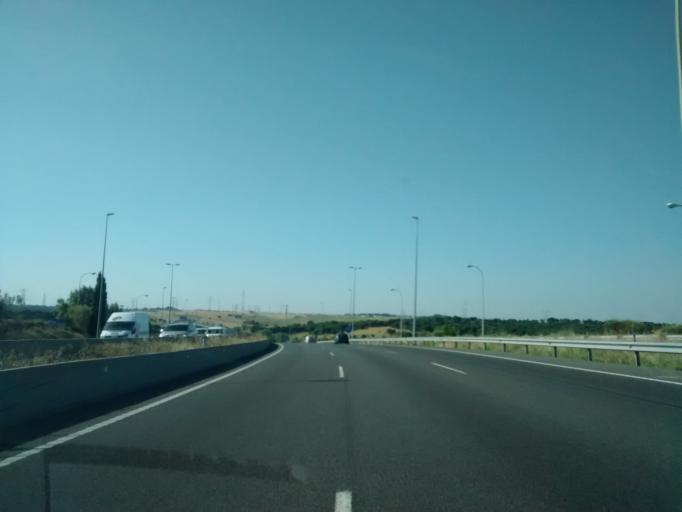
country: ES
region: Madrid
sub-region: Provincia de Madrid
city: Majadahonda
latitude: 40.4775
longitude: -3.8963
